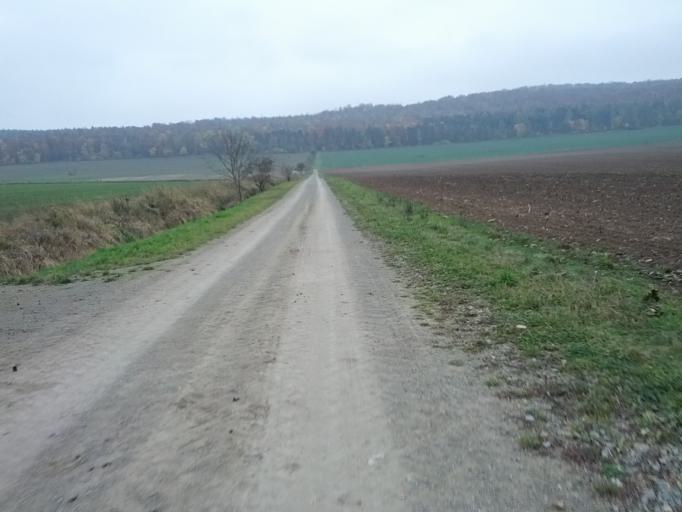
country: DE
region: Thuringia
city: Seebach
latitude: 50.9768
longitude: 10.4275
